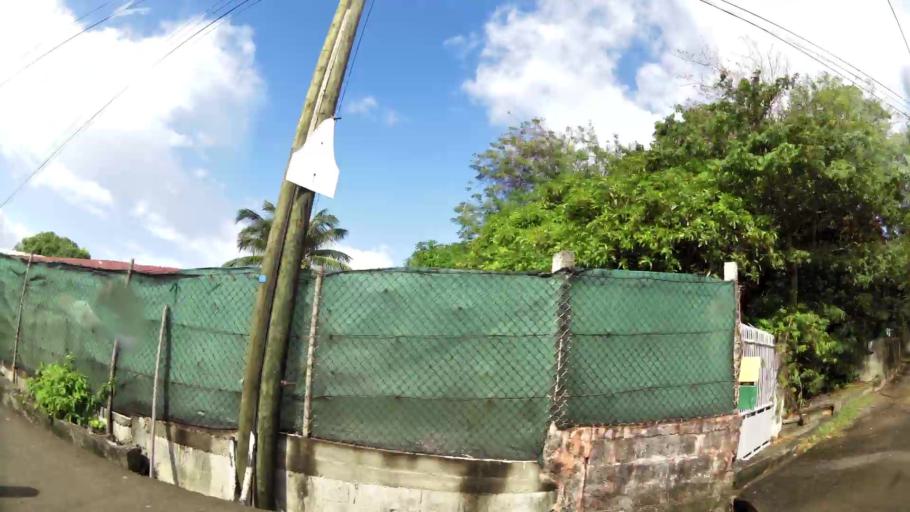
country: MQ
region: Martinique
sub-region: Martinique
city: Les Trois-Ilets
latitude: 14.5544
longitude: -61.0521
